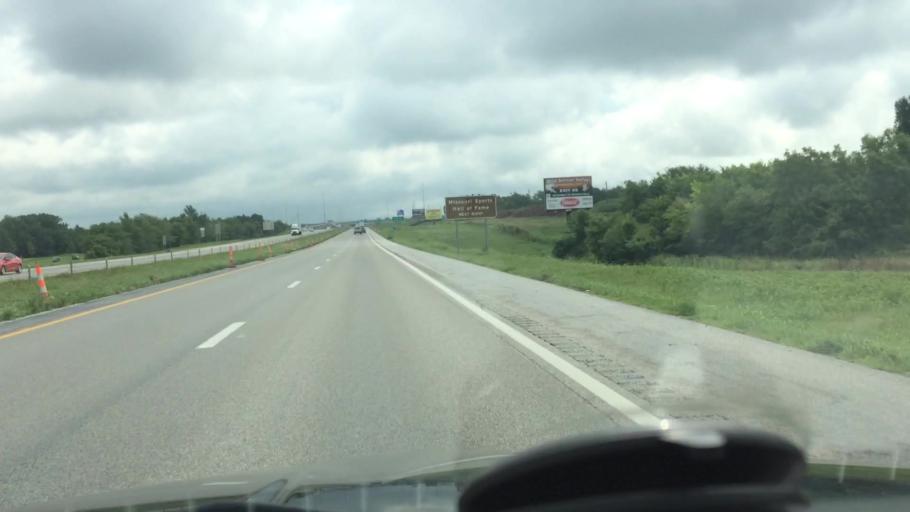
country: US
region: Missouri
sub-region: Greene County
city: Springfield
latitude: 37.2498
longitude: -93.2391
